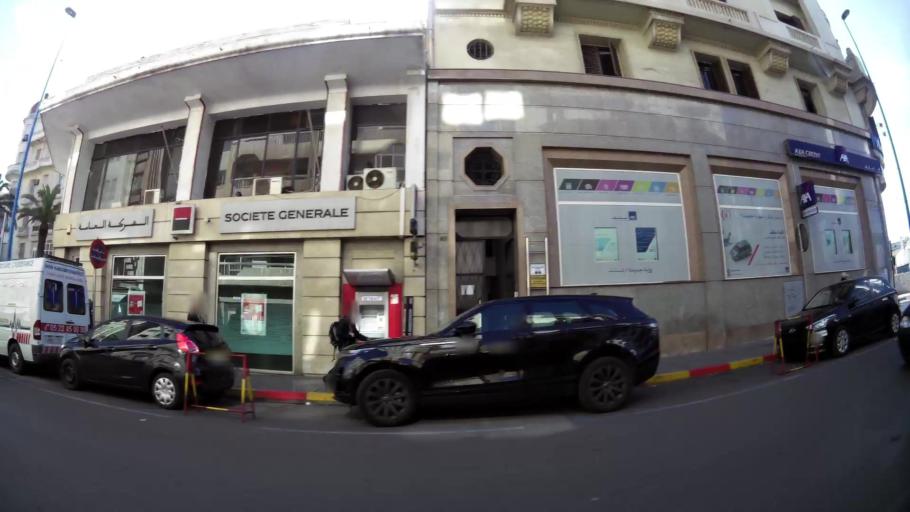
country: MA
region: Grand Casablanca
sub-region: Casablanca
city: Casablanca
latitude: 33.5944
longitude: -7.6104
